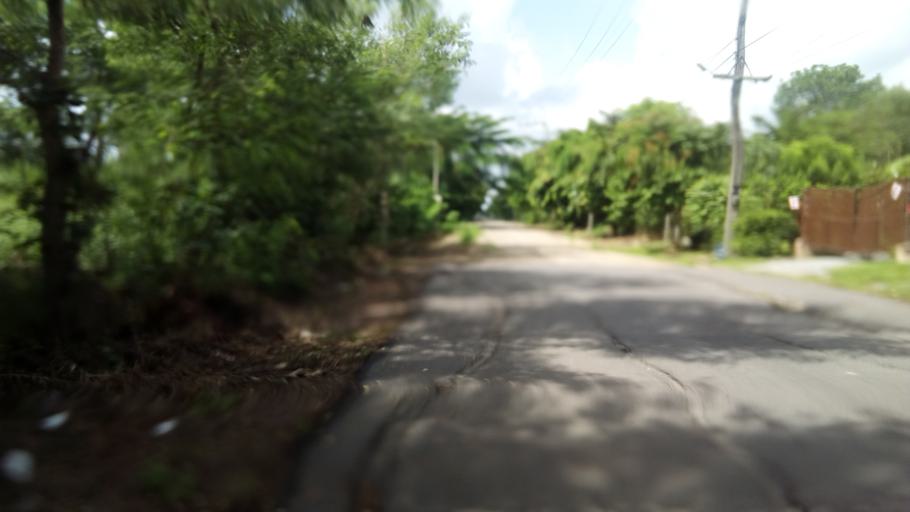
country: TH
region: Pathum Thani
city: Nong Suea
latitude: 14.0639
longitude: 100.8631
